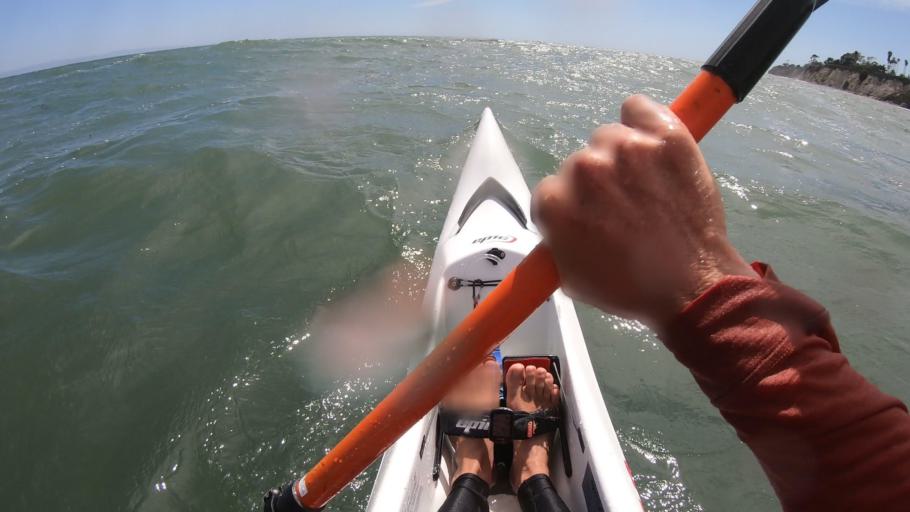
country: US
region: California
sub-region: Santa Barbara County
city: Santa Barbara
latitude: 34.3948
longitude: -119.7047
